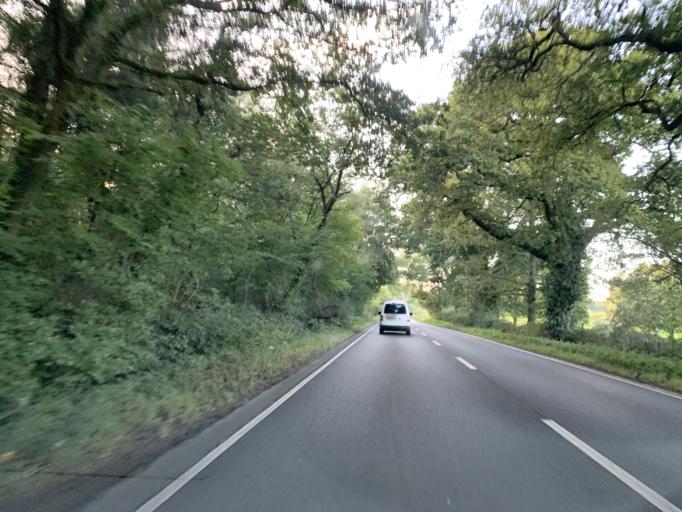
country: GB
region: England
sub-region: Hampshire
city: West Wellow
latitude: 50.9598
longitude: -1.5561
